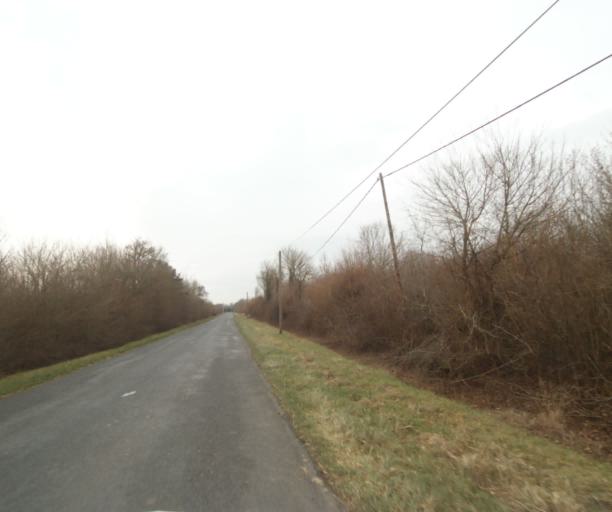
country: FR
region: Champagne-Ardenne
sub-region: Departement de la Haute-Marne
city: Villiers-en-Lieu
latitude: 48.6523
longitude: 4.8755
